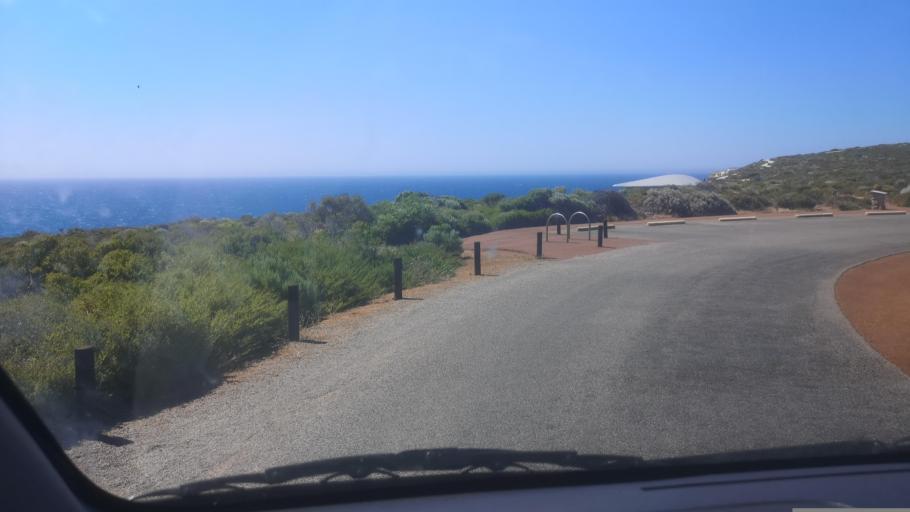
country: AU
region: Western Australia
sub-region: Northampton Shire
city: Kalbarri
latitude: -27.8275
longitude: 114.1131
